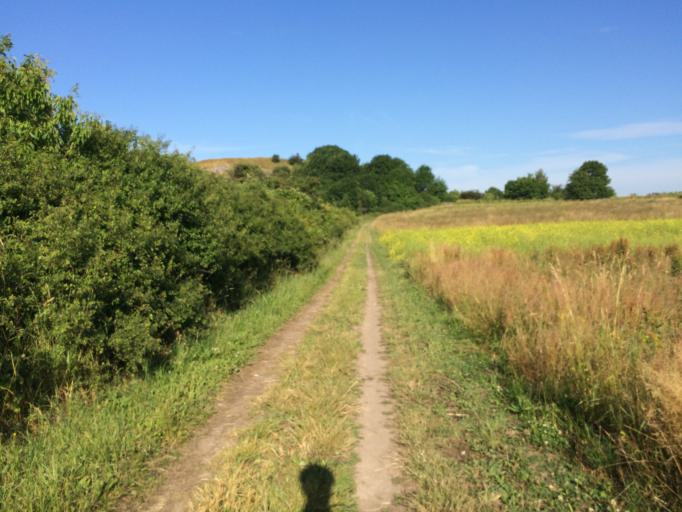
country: CZ
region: Central Bohemia
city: Horomerice
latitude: 50.0967
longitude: 14.3246
